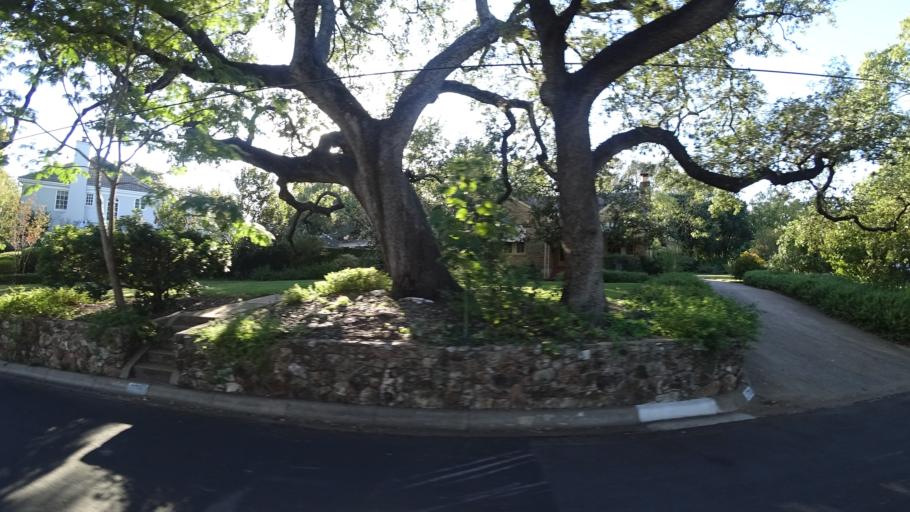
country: US
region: Texas
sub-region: Travis County
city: Austin
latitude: 30.2971
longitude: -97.7509
